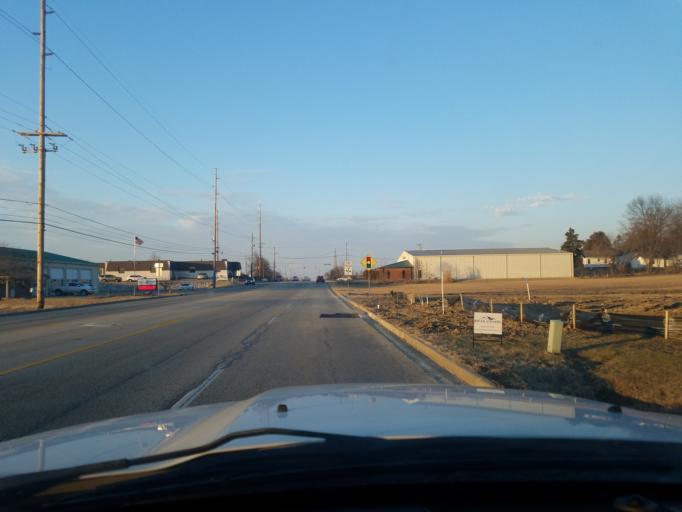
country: US
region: Indiana
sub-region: Vanderburgh County
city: Melody Hill
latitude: 38.0004
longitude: -87.4738
